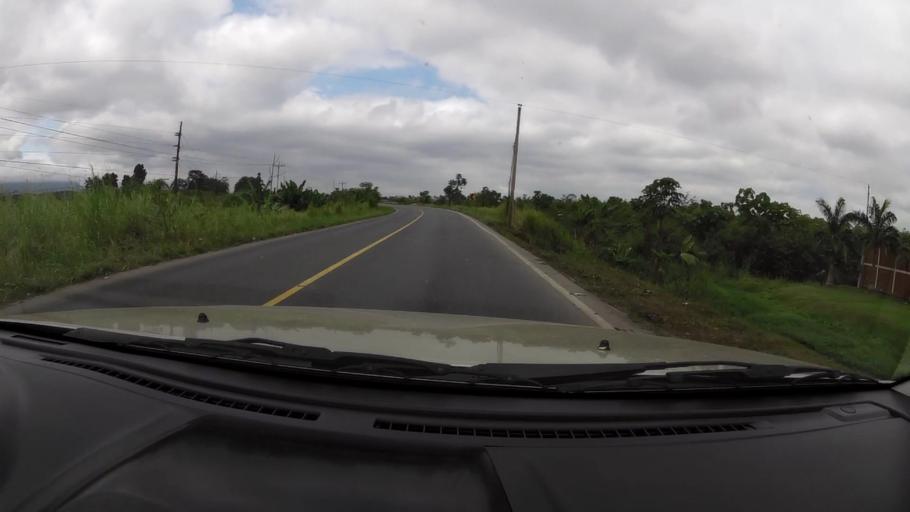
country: EC
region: Guayas
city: Naranjal
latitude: -2.6889
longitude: -79.6393
